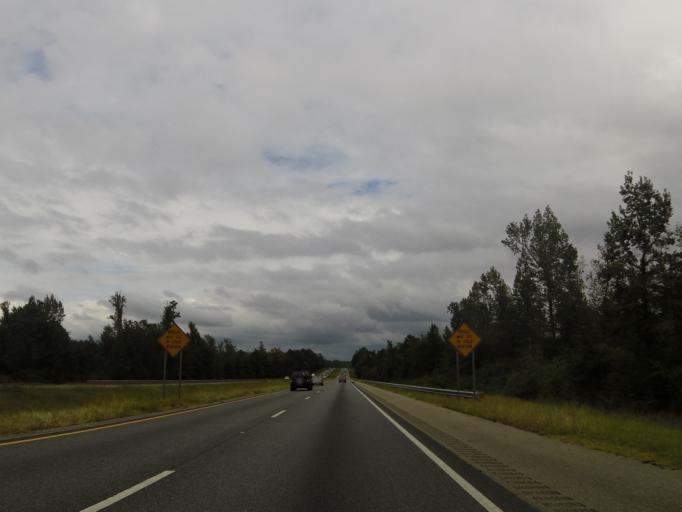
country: US
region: Alabama
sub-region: Escambia County
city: Brewton
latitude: 31.2937
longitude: -87.1821
